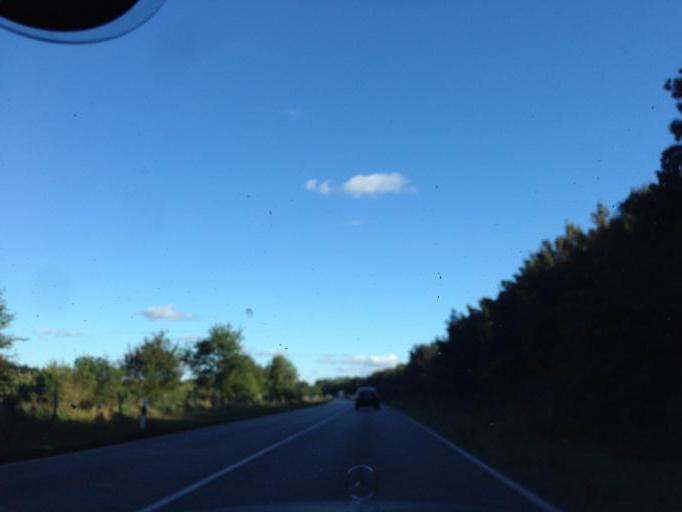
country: DE
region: Schleswig-Holstein
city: Boostedt
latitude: 54.0290
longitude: 10.0441
